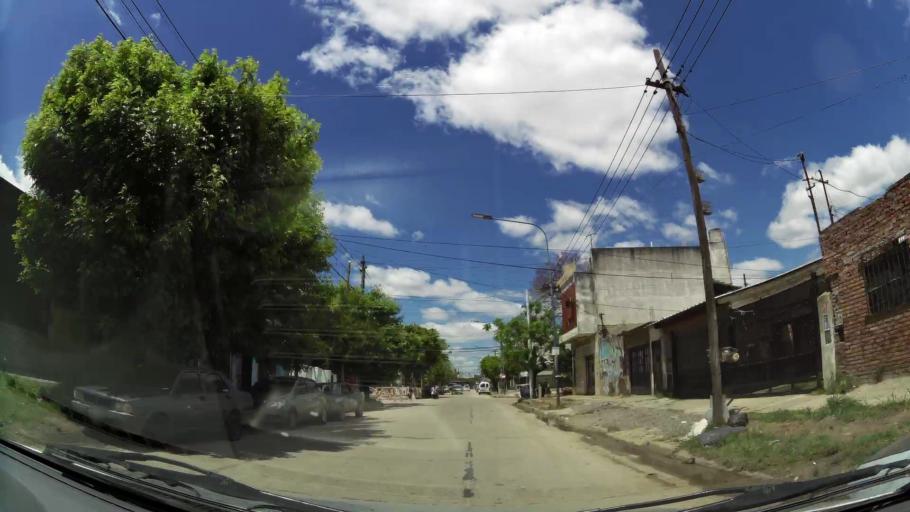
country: AR
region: Buenos Aires
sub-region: Partido de Lanus
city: Lanus
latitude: -34.7079
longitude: -58.4206
